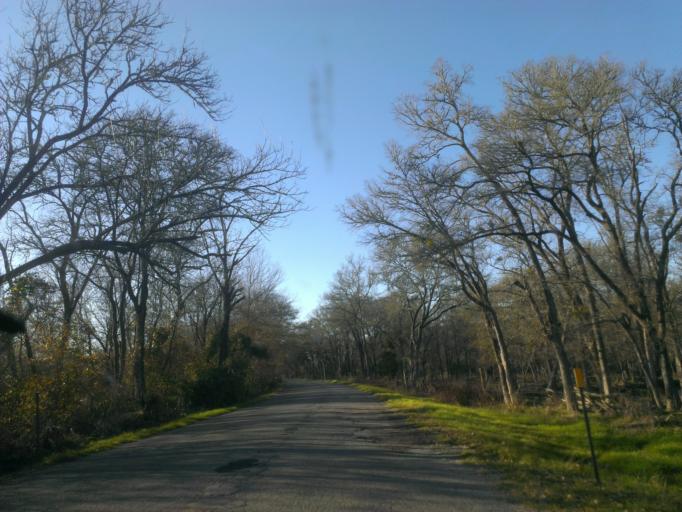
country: US
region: Texas
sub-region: Bastrop County
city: Elgin
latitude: 30.3581
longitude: -97.3148
